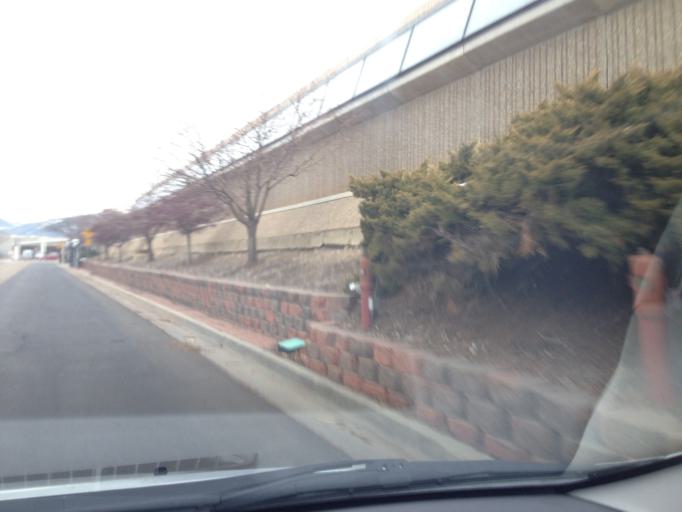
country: US
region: Colorado
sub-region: Boulder County
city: Boulder
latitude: 40.0162
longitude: -105.2482
